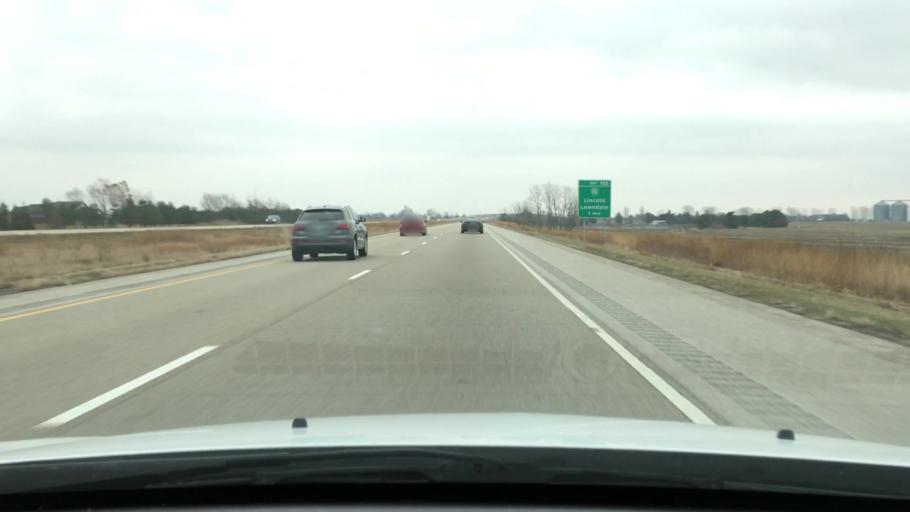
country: US
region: Illinois
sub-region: Logan County
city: Lincoln
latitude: 40.1831
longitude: -89.3399
